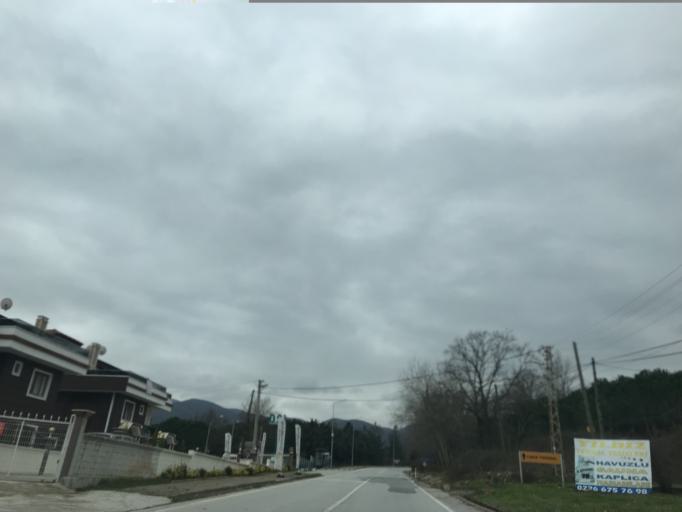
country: TR
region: Yalova
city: Termal
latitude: 40.6062
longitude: 29.1966
